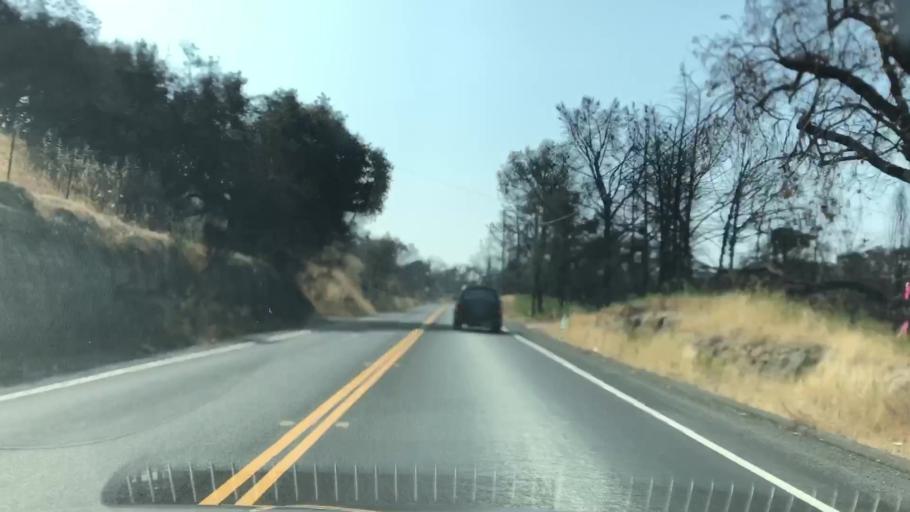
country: US
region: California
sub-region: Sonoma County
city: Larkfield-Wikiup
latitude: 38.5235
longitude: -122.7191
